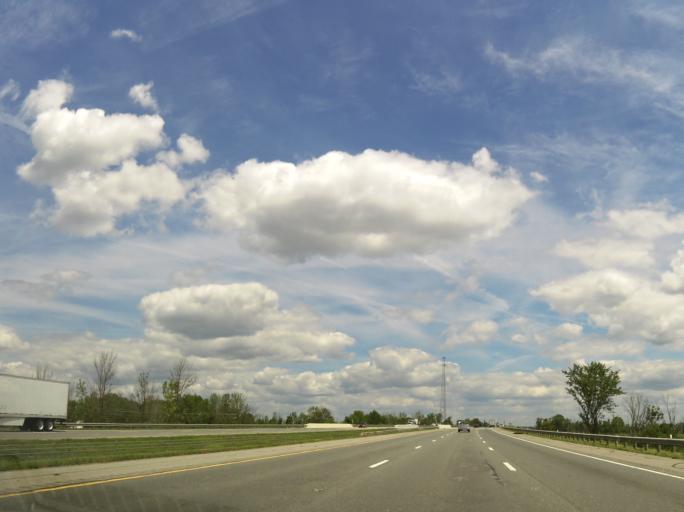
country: US
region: Ohio
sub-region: Medina County
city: Lodi
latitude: 40.9854
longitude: -82.0369
